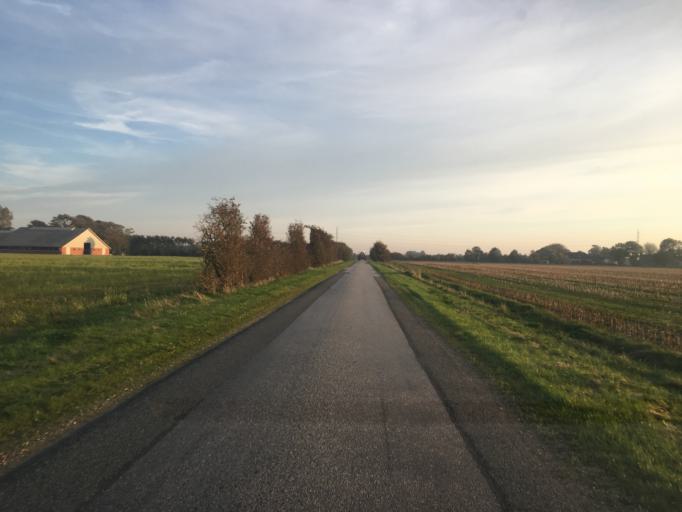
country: DK
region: South Denmark
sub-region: Tonder Kommune
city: Logumkloster
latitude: 55.0436
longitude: 9.0267
